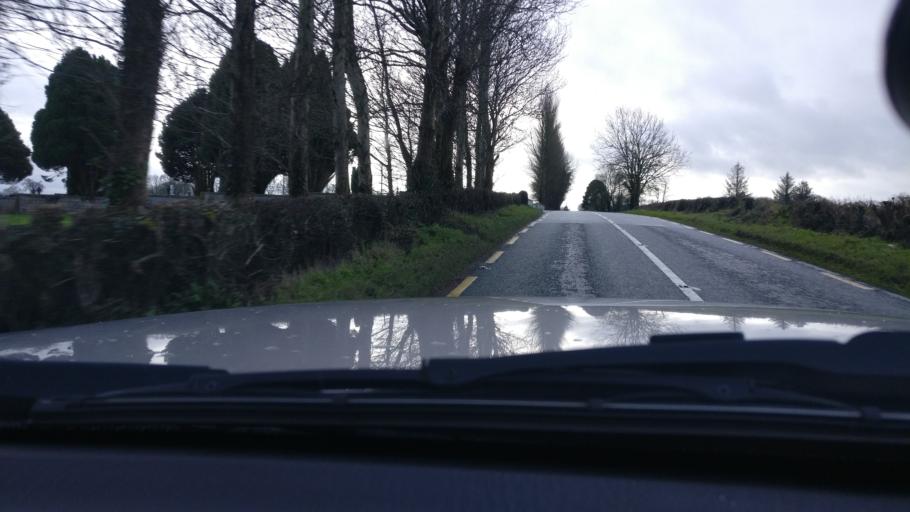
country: IE
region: Leinster
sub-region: An Iarmhi
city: Moate
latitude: 53.6051
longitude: -7.7112
